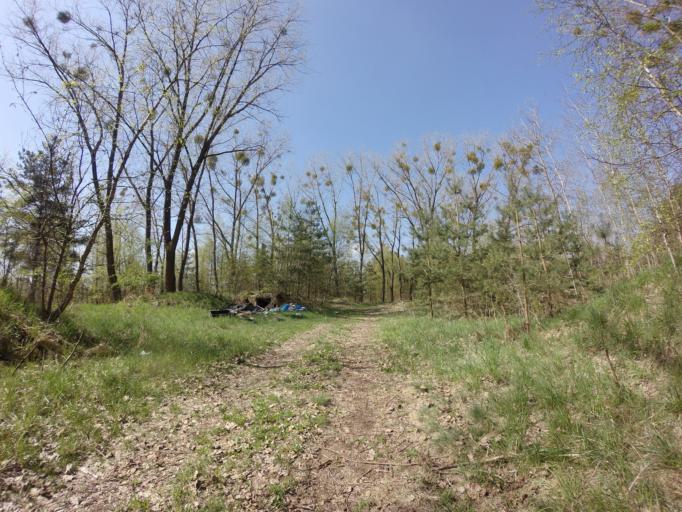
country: PL
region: West Pomeranian Voivodeship
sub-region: Powiat choszczenski
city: Choszczno
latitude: 53.1589
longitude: 15.4566
